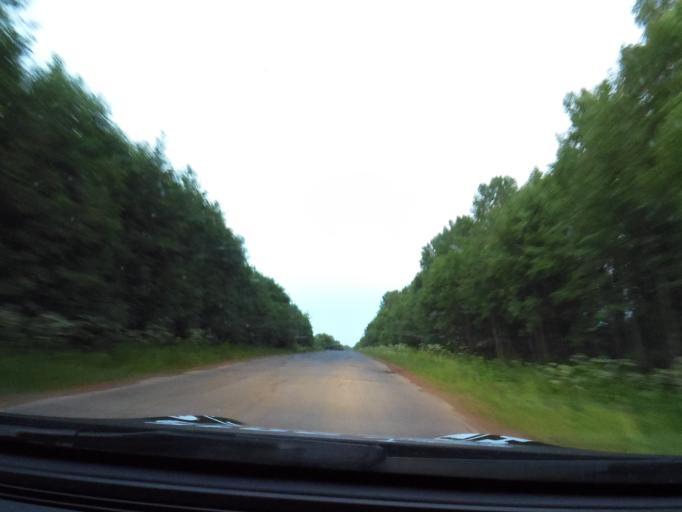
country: RU
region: Vologda
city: Vytegra
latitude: 61.0019
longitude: 36.3125
